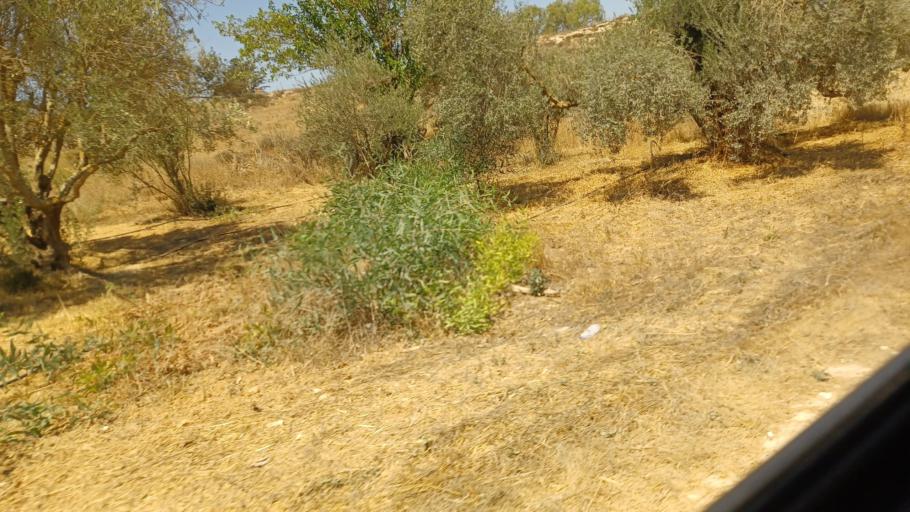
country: CY
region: Ammochostos
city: Acheritou
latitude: 35.0792
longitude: 33.8908
